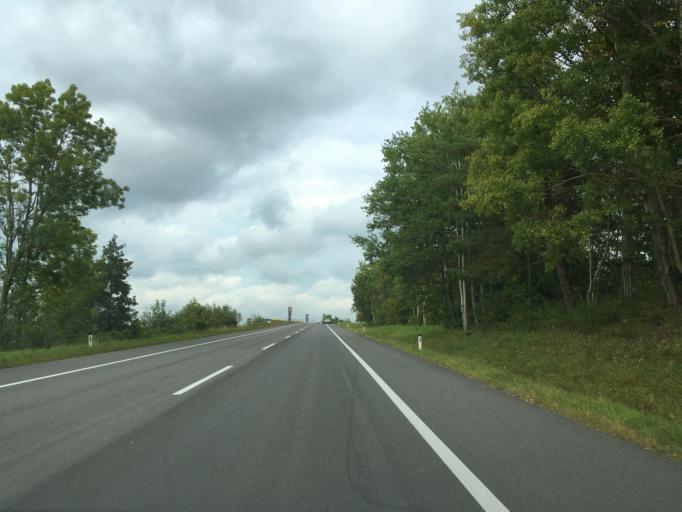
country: AT
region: Styria
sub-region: Politischer Bezirk Hartberg-Fuerstenfeld
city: Friedberg
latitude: 47.4258
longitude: 16.0573
